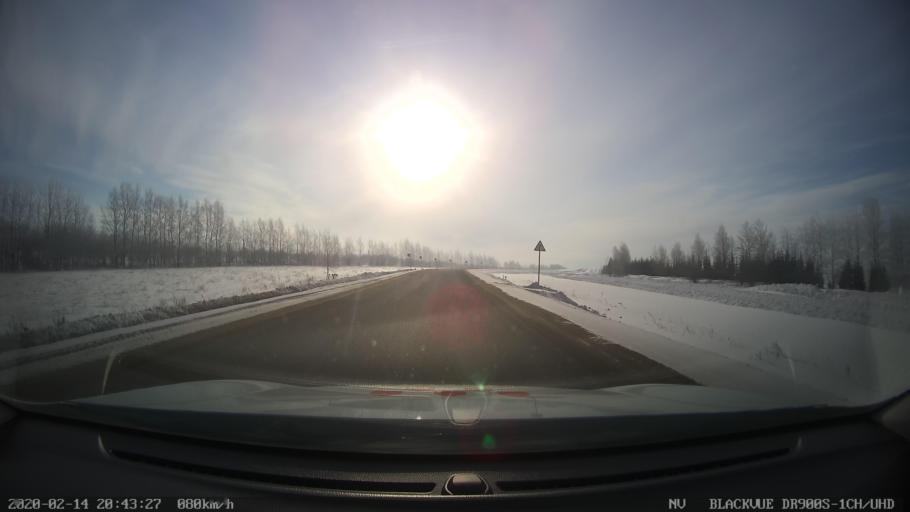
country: RU
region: Tatarstan
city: Kuybyshevskiy Zaton
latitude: 55.3078
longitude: 49.1480
